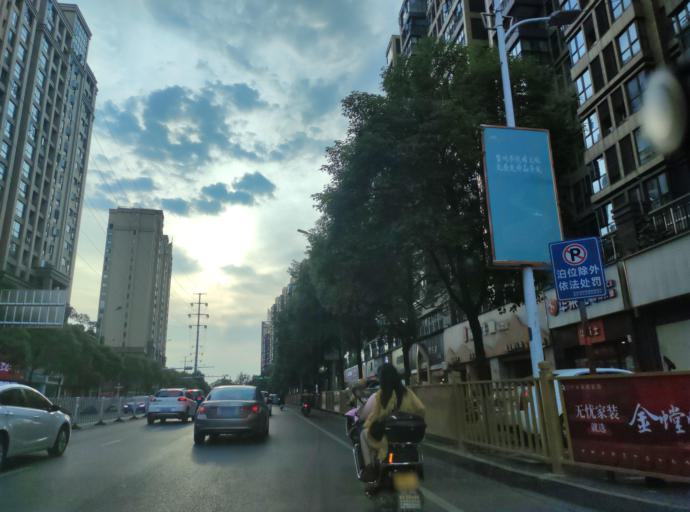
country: CN
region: Jiangxi Sheng
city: Pingxiang
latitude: 27.6335
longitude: 113.8677
